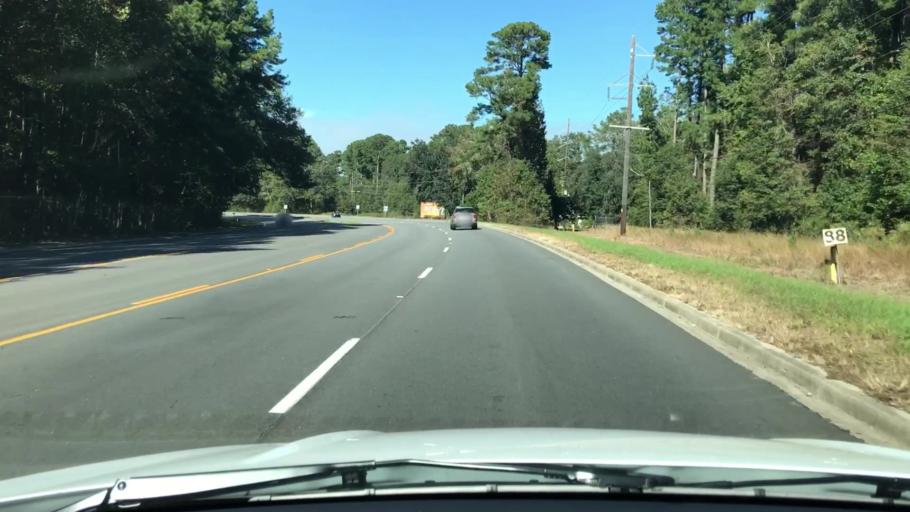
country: US
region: South Carolina
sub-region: Beaufort County
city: Laurel Bay
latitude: 32.5836
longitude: -80.7429
